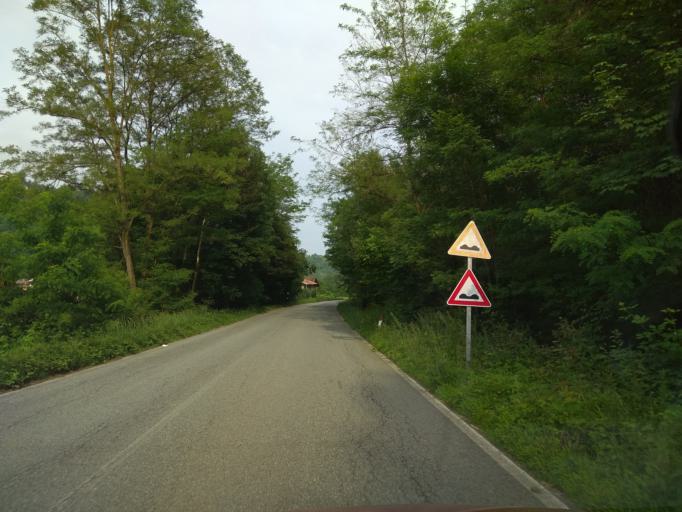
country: IT
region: Piedmont
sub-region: Provincia di Biella
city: Coggiola
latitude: 45.6817
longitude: 8.1878
